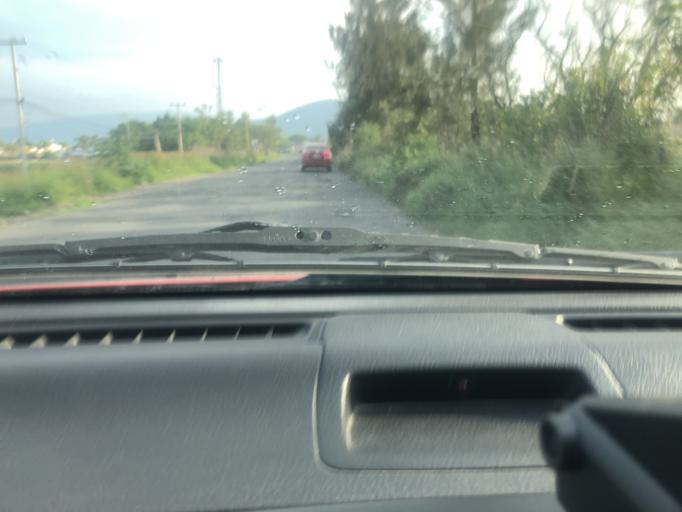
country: MX
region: Jalisco
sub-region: San Pedro Tlaquepaque
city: Santa Anita
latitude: 20.5562
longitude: -103.4179
